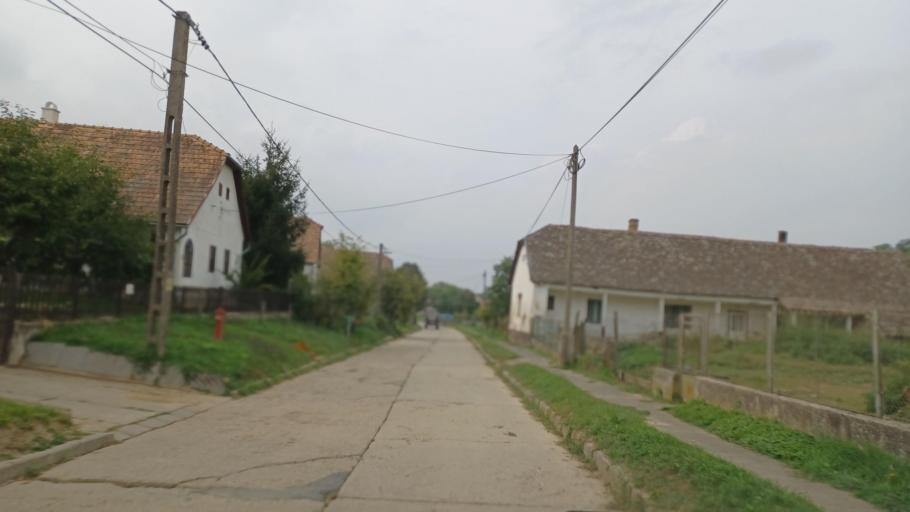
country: HU
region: Tolna
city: Gyonk
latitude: 46.5704
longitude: 18.4275
